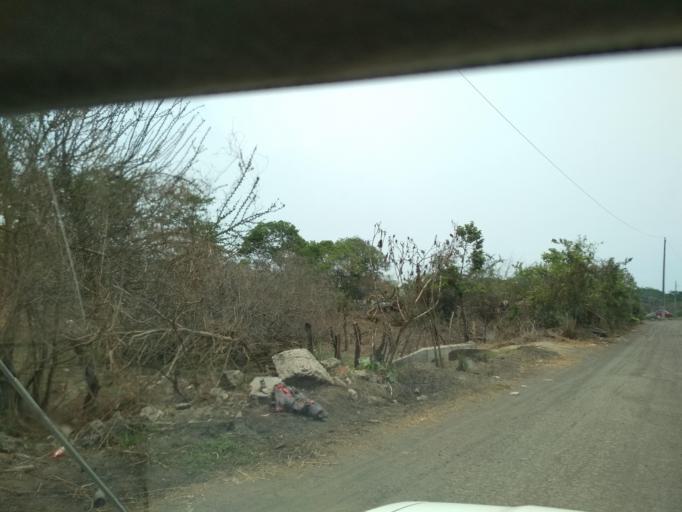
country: MX
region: Veracruz
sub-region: Veracruz
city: Delfino Victoria (Santa Fe)
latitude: 19.2006
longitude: -96.2639
